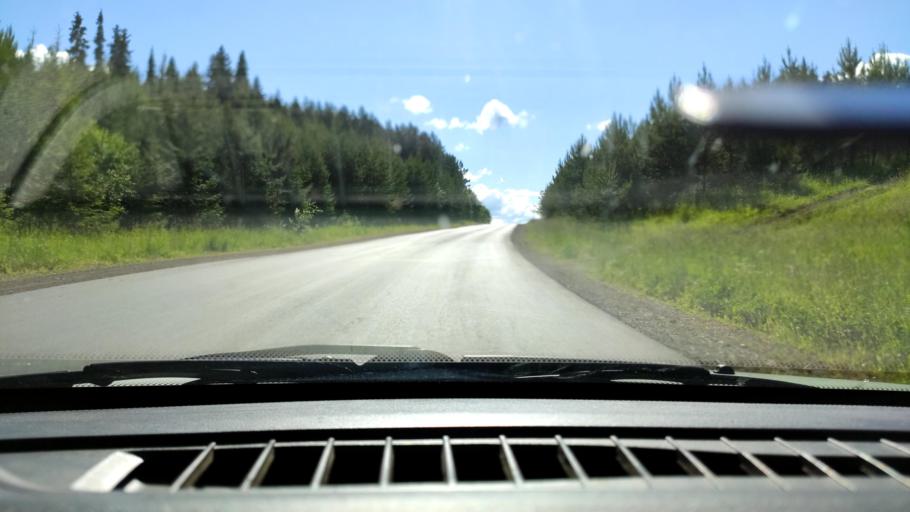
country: RU
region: Perm
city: Uinskoye
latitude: 57.1142
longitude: 56.5434
